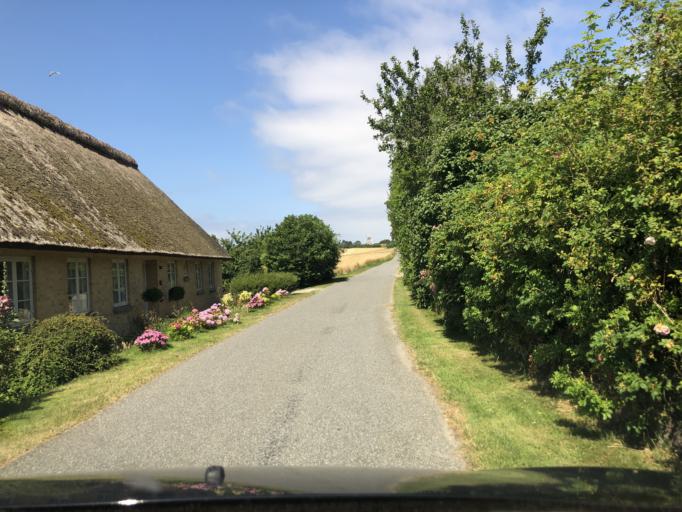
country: DK
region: South Denmark
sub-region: AEro Kommune
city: AEroskobing
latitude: 54.9193
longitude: 10.2908
